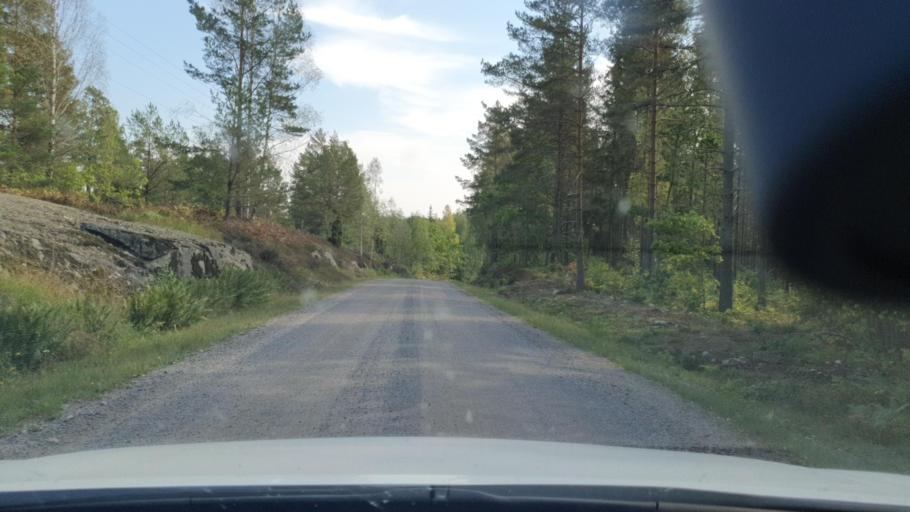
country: SE
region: Kalmar
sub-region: Vasterviks Kommun
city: Ankarsrum
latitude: 57.6964
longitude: 16.4628
